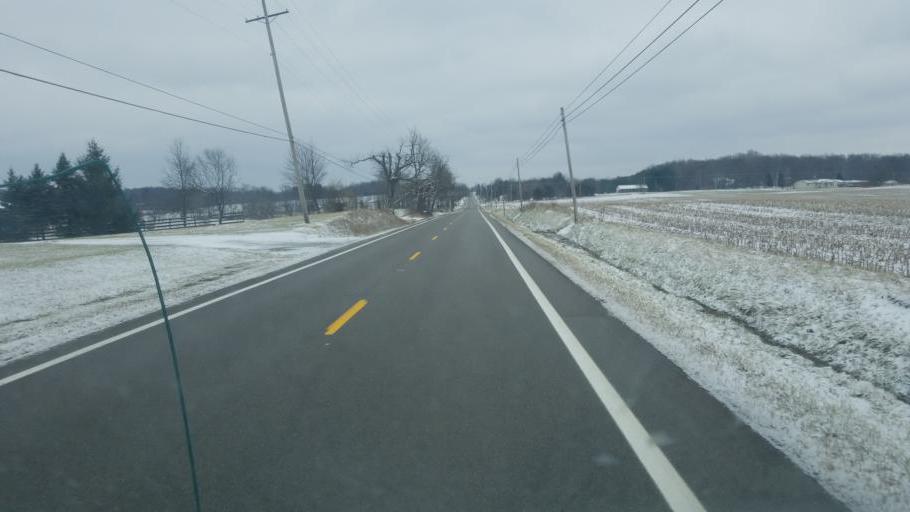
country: US
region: Ohio
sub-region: Licking County
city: Johnstown
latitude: 40.1708
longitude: -82.7137
